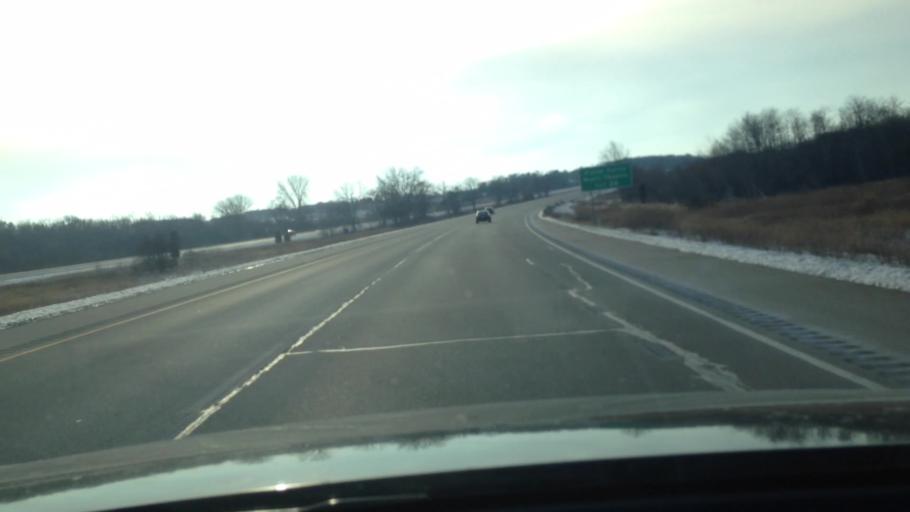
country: US
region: Wisconsin
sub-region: Walworth County
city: East Troy
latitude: 42.7793
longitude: -88.3934
